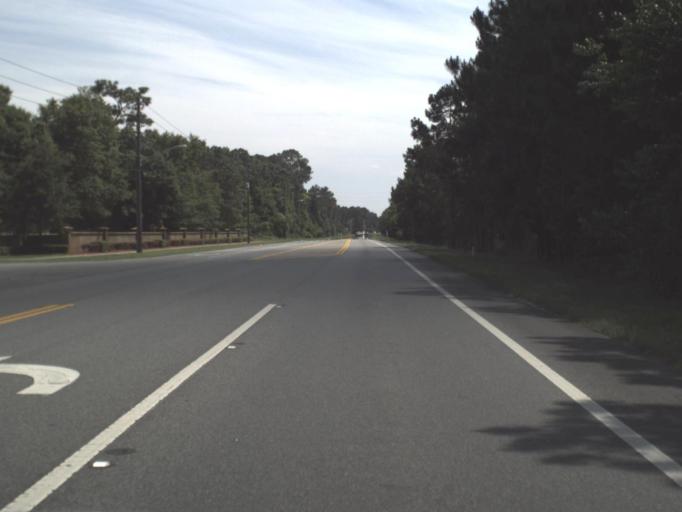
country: US
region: Florida
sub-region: Nassau County
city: Yulee
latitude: 30.5043
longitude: -81.6229
